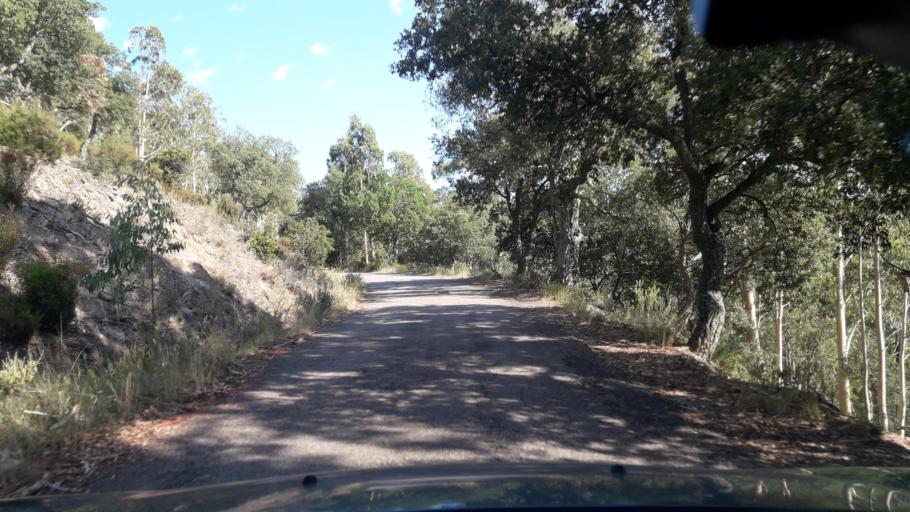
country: FR
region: Provence-Alpes-Cote d'Azur
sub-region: Departement du Var
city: Saint-Raphael
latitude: 43.4983
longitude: 6.7996
